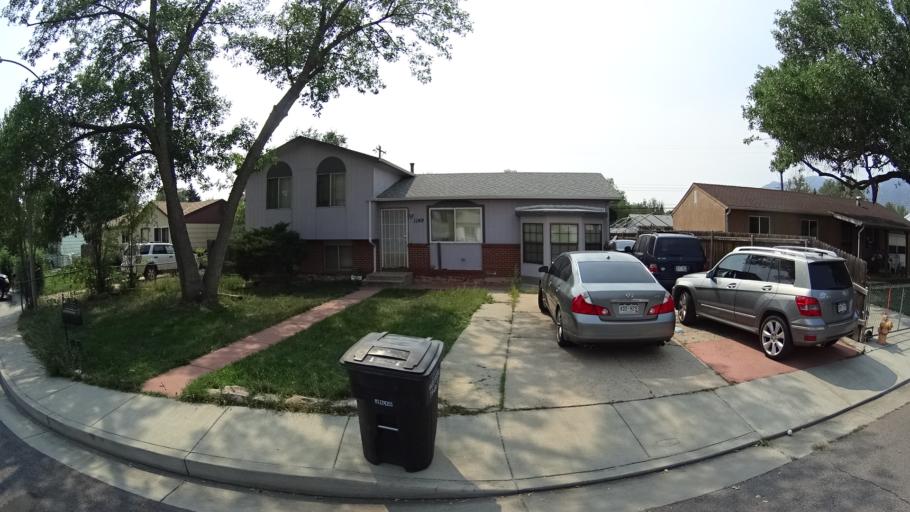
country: US
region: Colorado
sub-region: El Paso County
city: Colorado Springs
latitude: 38.8009
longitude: -104.8085
